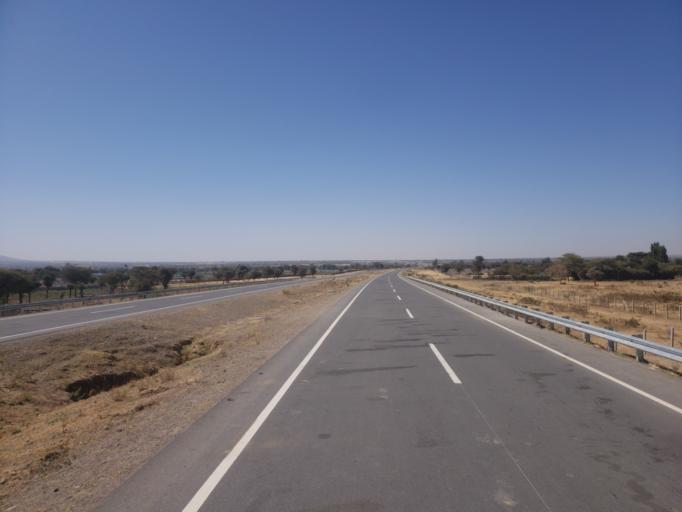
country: ET
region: Oromiya
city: Mojo
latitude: 8.3517
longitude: 38.9834
